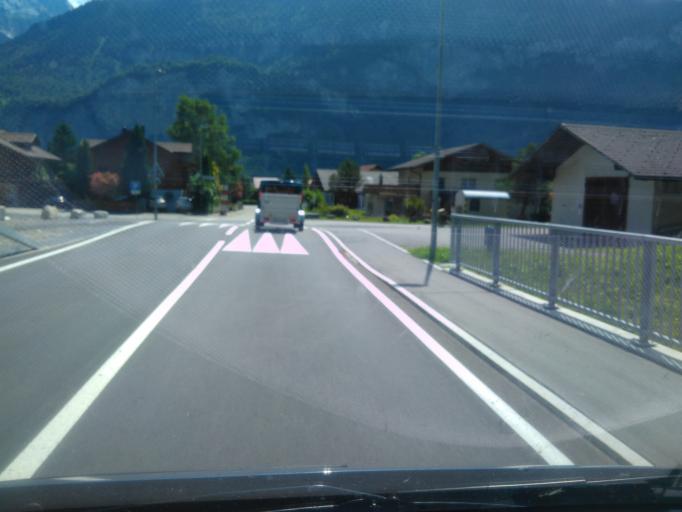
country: CH
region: Bern
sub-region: Interlaken-Oberhasli District
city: Meiringen
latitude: 46.7385
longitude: 8.1679
